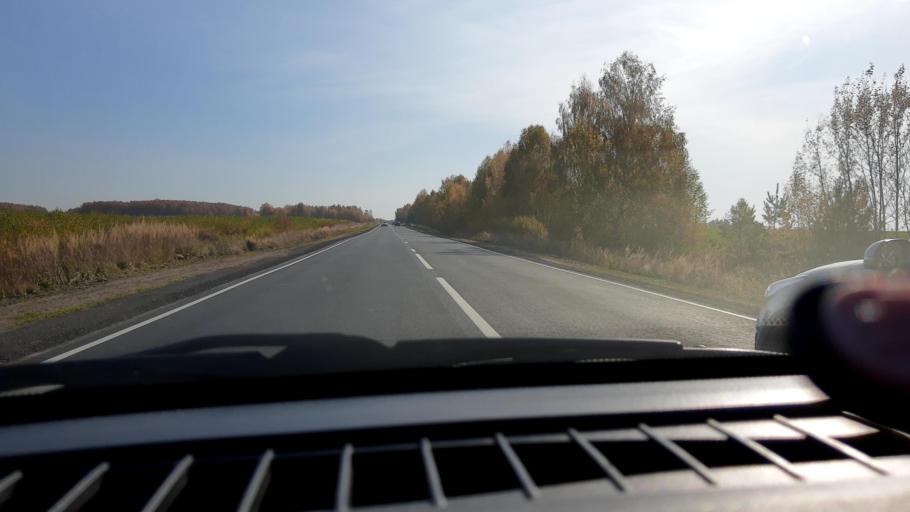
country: RU
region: Nizjnij Novgorod
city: Novaya Balakhna
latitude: 56.5813
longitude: 43.6858
